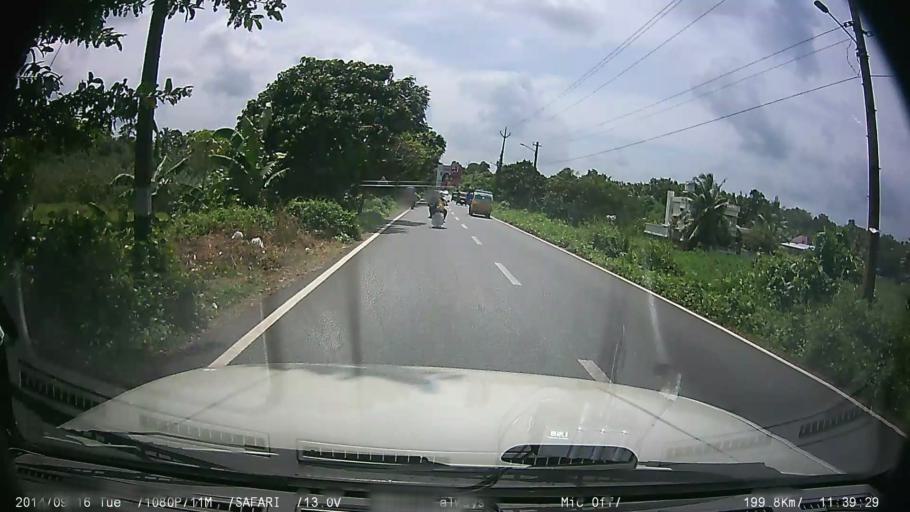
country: IN
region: Kerala
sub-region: Kottayam
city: Changanacheri
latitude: 9.4490
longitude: 76.5476
